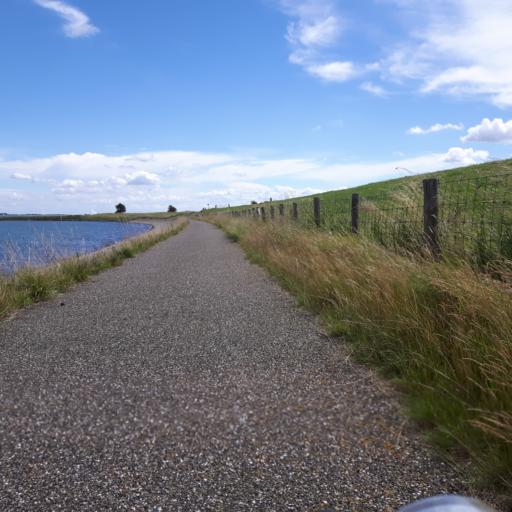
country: NL
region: Zeeland
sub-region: Gemeente Goes
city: Goes
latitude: 51.5650
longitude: 3.8955
